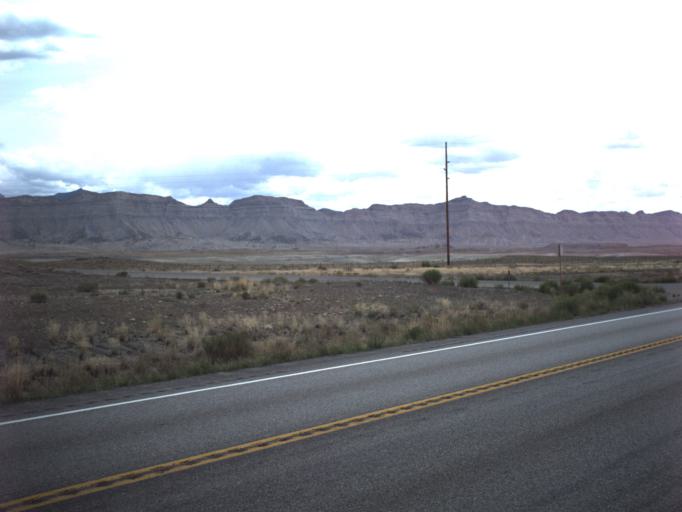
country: US
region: Utah
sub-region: Carbon County
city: East Carbon City
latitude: 39.3704
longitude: -110.3972
